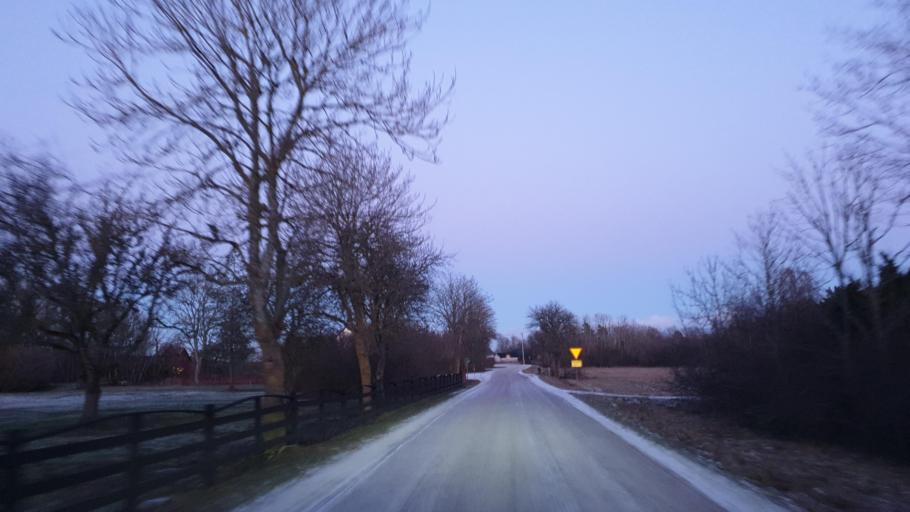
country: SE
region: Gotland
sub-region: Gotland
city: Slite
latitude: 57.4248
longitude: 18.8308
